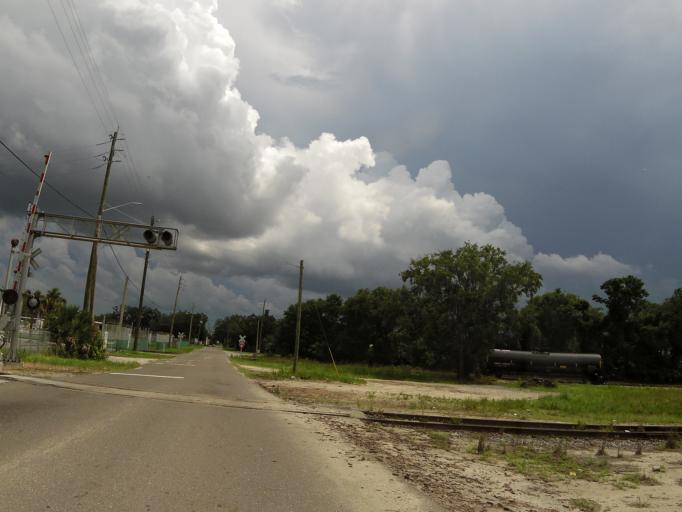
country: US
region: Florida
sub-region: Duval County
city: Jacksonville
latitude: 30.3776
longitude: -81.6414
